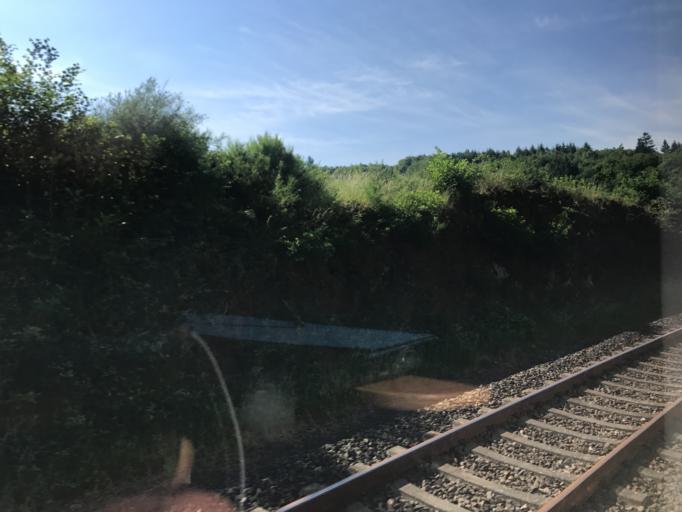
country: DE
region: Rheinland-Pfalz
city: Frauenberg
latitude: 49.6821
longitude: 7.2896
